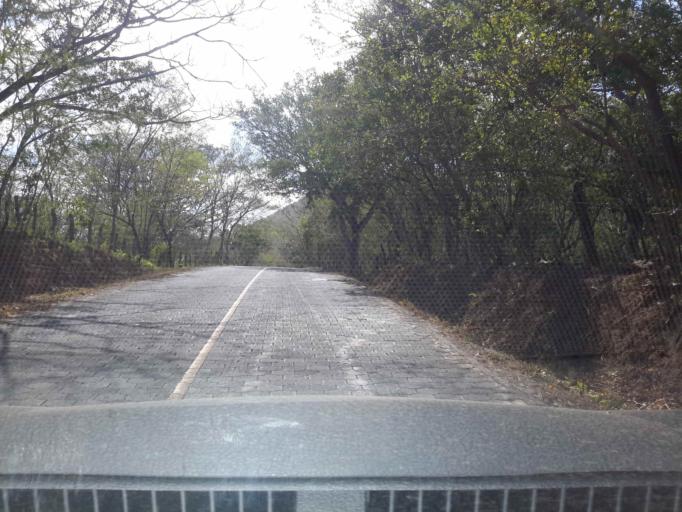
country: NI
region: Rivas
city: San Juan del Sur
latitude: 11.2410
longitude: -85.8342
